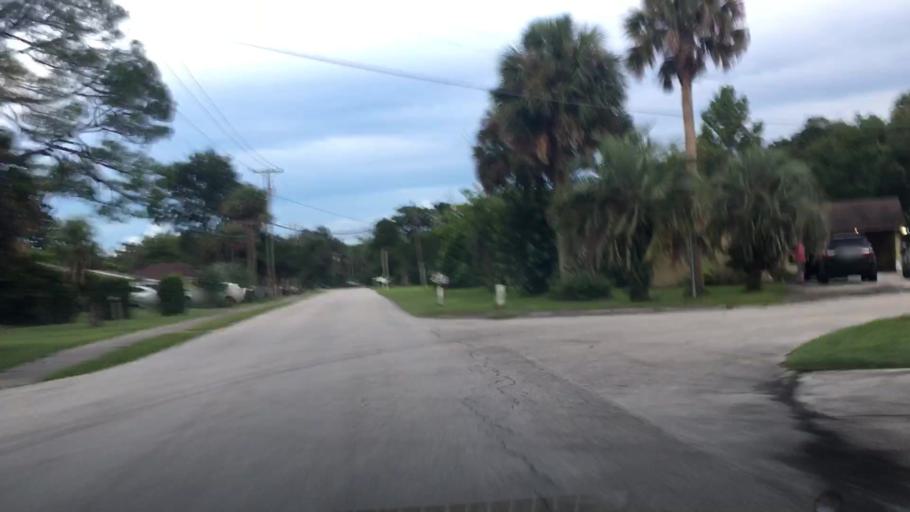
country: US
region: Florida
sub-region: Volusia County
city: DeBary
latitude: 28.8768
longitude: -81.2989
